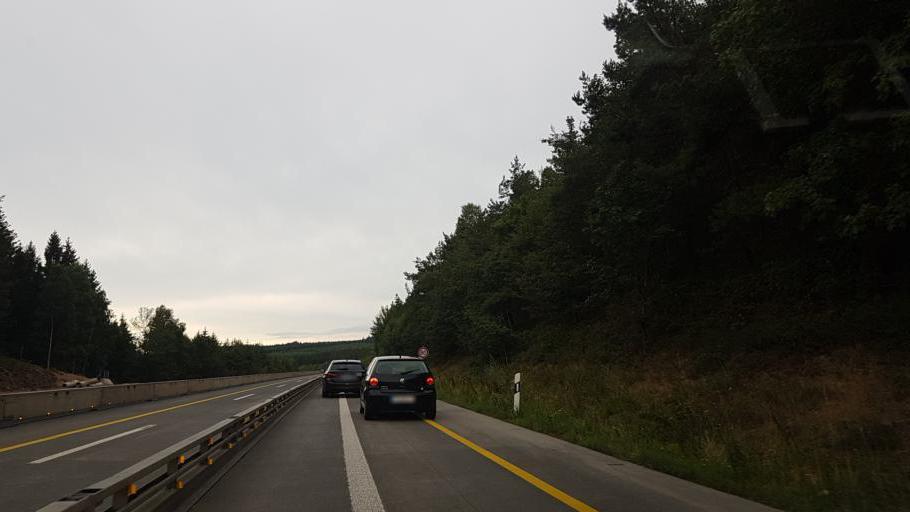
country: DE
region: Rheinland-Pfalz
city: Bescheid
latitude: 49.7304
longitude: 6.8891
